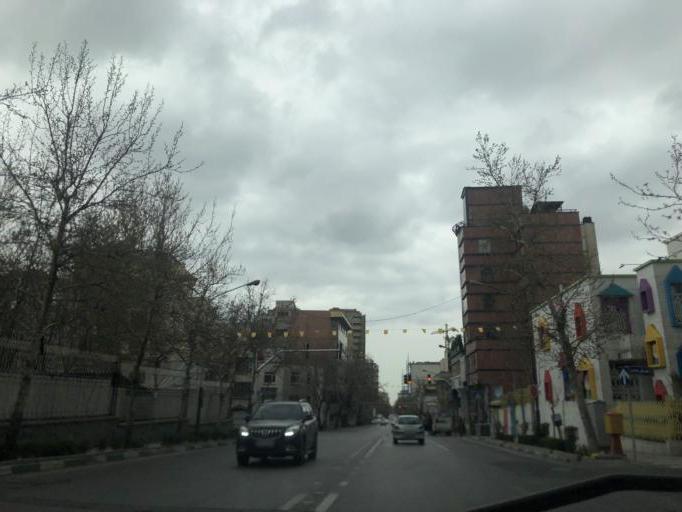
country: IR
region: Tehran
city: Tajrish
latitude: 35.7768
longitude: 51.4655
